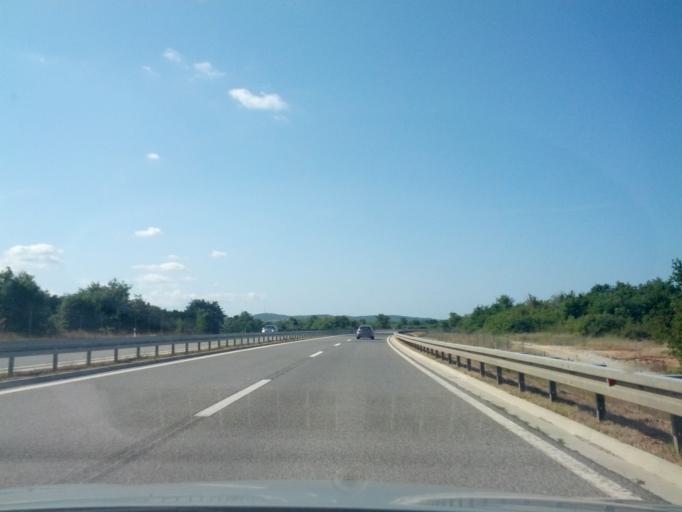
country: HR
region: Istarska
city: Vrsar
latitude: 45.1757
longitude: 13.7338
